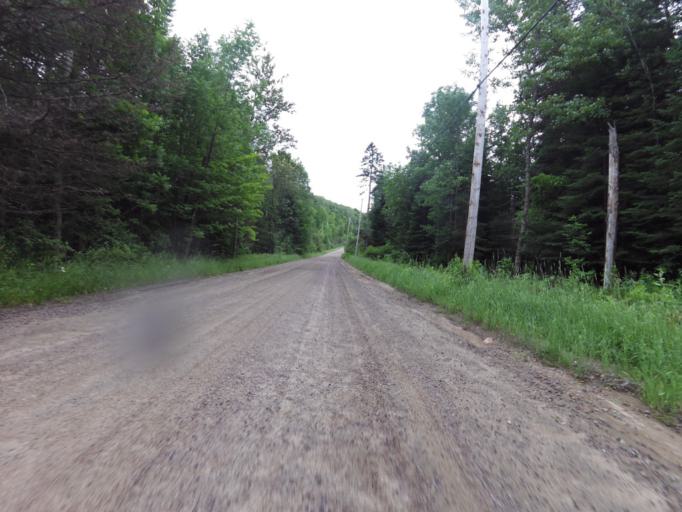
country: CA
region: Quebec
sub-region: Laurentides
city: Mont-Tremblant
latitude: 45.9169
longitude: -74.5998
